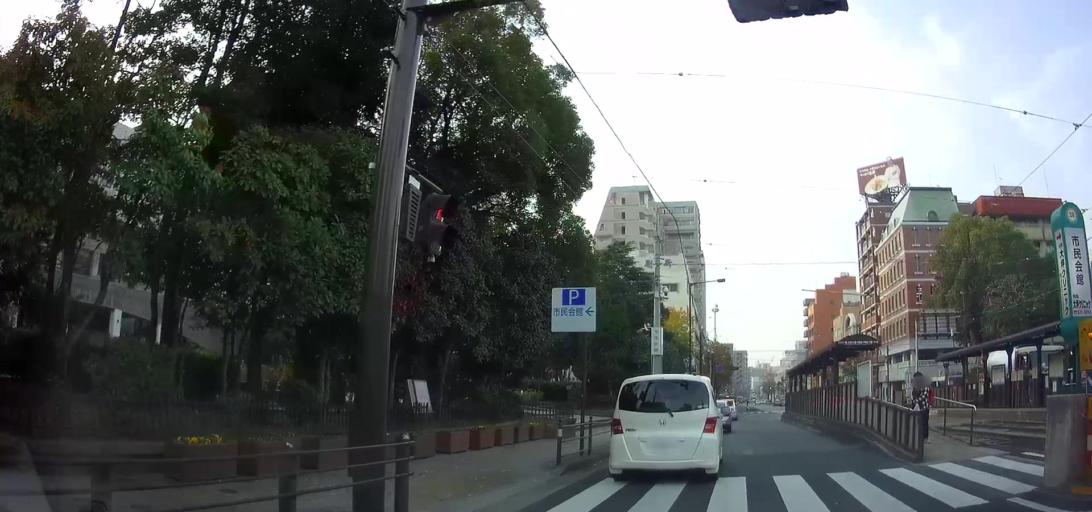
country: JP
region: Nagasaki
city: Nagasaki-shi
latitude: 32.7492
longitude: 129.8811
